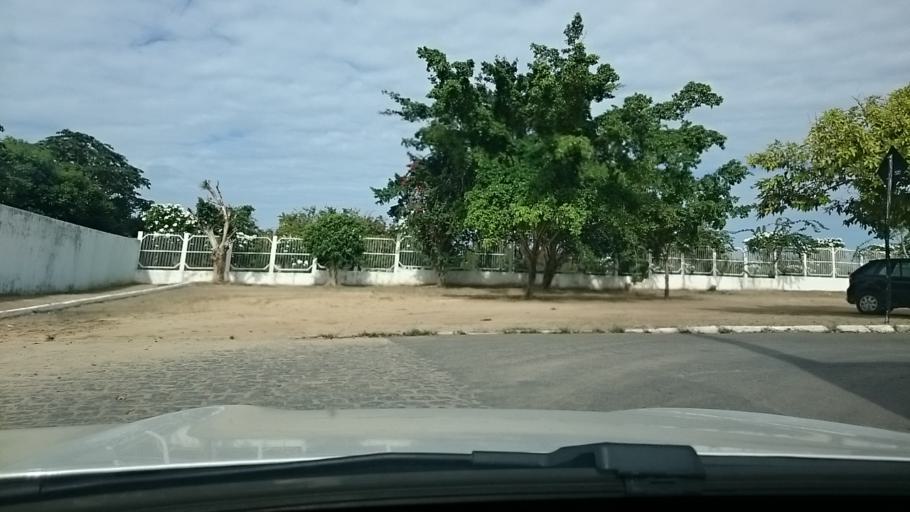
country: BR
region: Paraiba
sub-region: Joao Pessoa
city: Joao Pessoa
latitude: -7.1707
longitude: -34.8538
